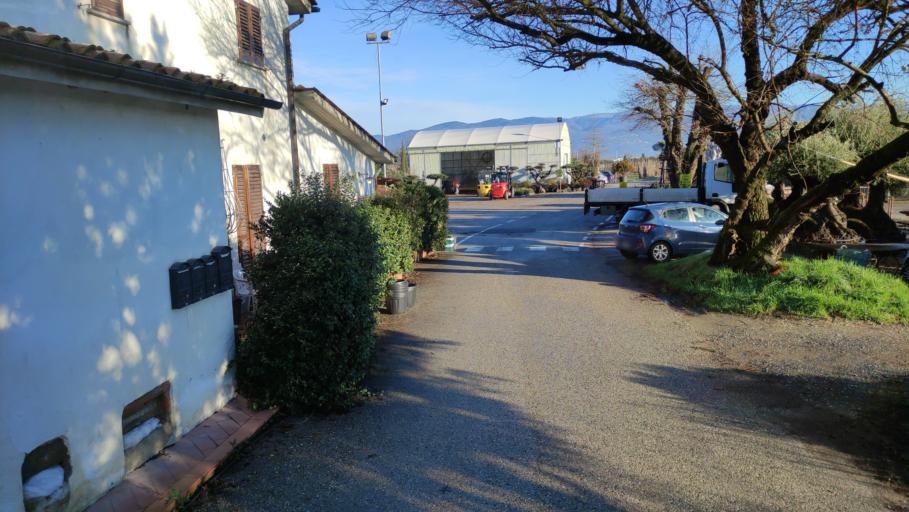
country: IT
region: Tuscany
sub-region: Provincia di Pistoia
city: Cantagrillo-Casalguidi
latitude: 43.8732
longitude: 10.9369
